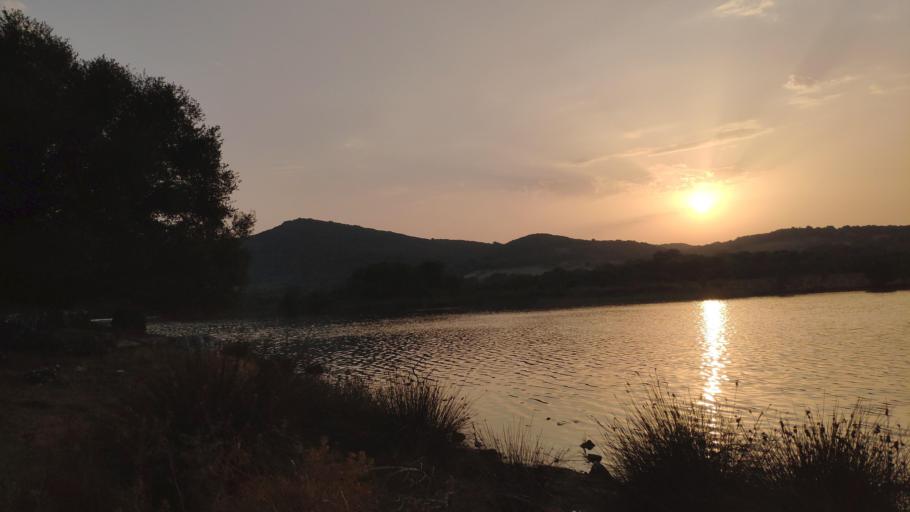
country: GR
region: West Greece
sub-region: Nomos Aitolias kai Akarnanias
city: Monastirakion
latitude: 38.9196
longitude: 20.9952
